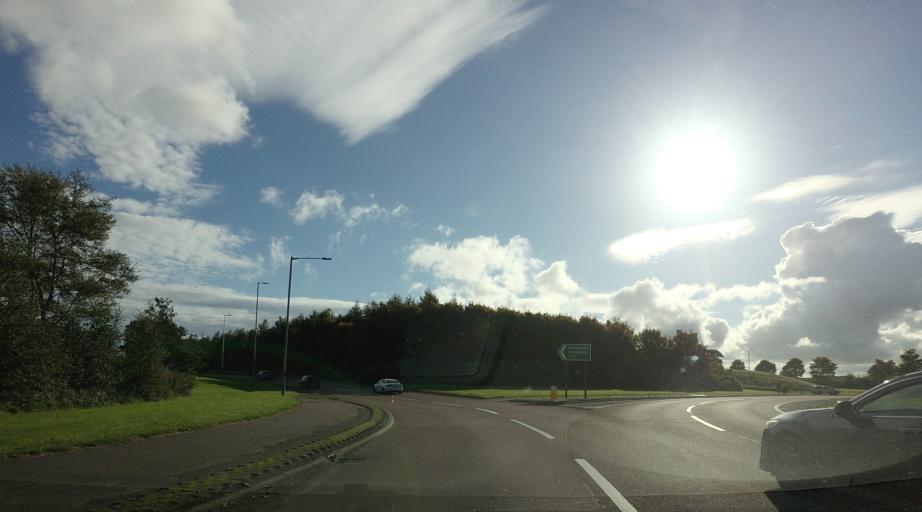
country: GB
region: Scotland
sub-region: Fife
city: Thornton
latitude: 56.1816
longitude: -3.1466
